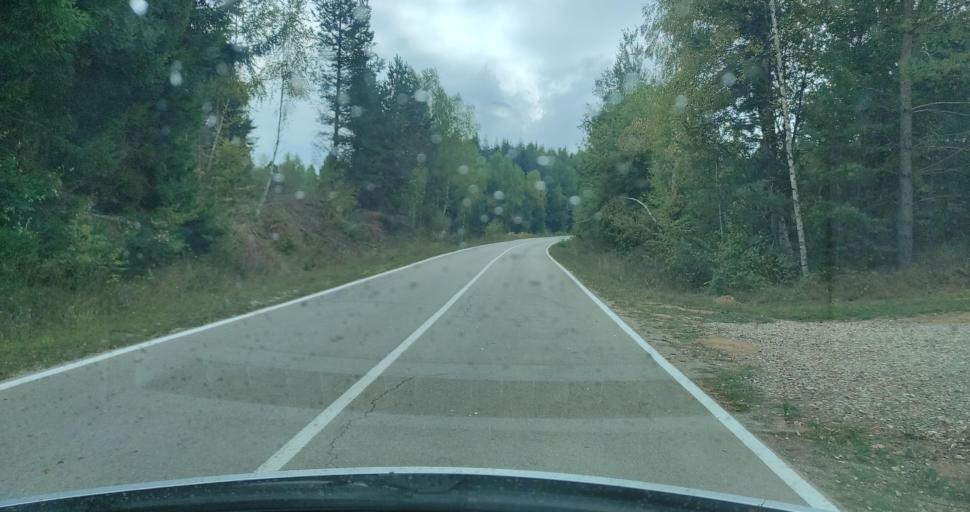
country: RS
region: Central Serbia
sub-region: Jablanicki Okrug
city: Crna Trava
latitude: 42.6831
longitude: 22.3140
